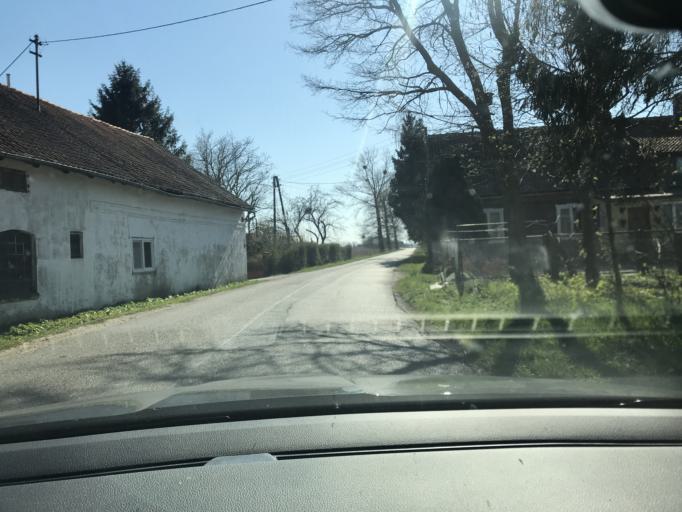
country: PL
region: Pomeranian Voivodeship
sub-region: Powiat nowodworski
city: Sztutowo
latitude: 54.3113
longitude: 19.1600
